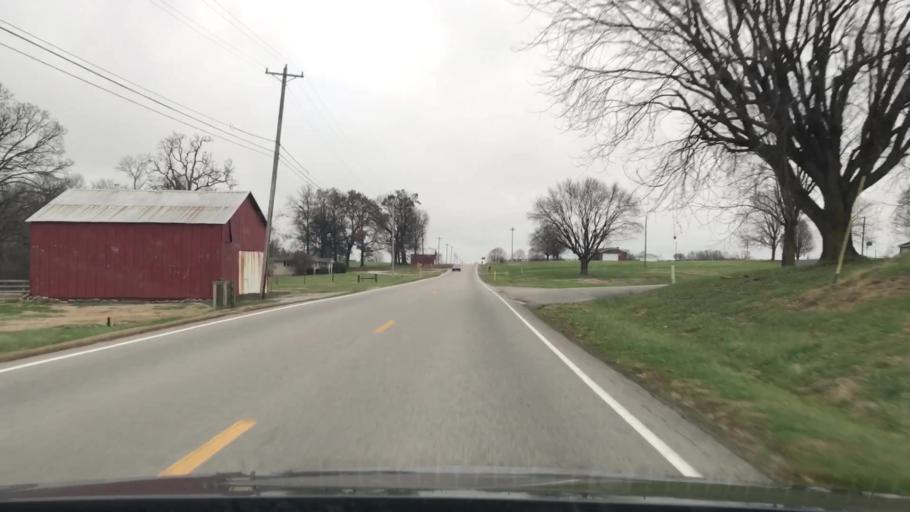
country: US
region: Kentucky
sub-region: Todd County
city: Elkton
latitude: 36.7600
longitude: -87.1673
